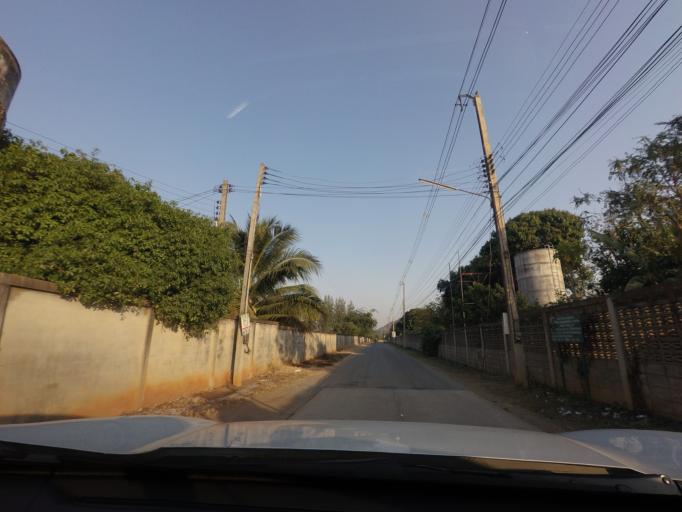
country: TH
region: Nakhon Ratchasima
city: Pak Chong
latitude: 14.6424
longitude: 101.3579
